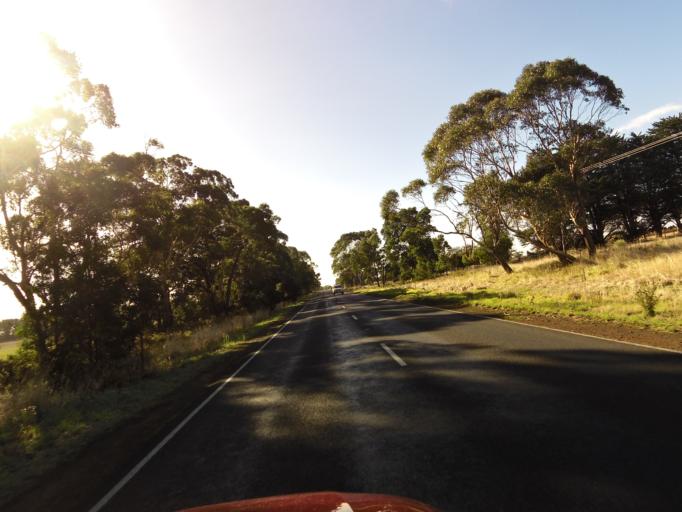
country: AU
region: Victoria
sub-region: Warrnambool
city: Allansford
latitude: -38.3979
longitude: 142.9518
